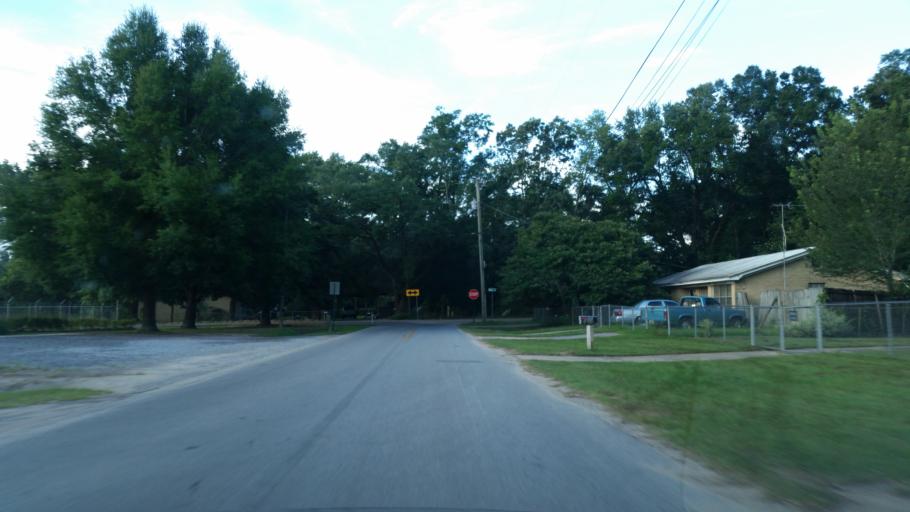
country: US
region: Florida
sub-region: Escambia County
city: Ensley
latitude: 30.5278
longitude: -87.3050
